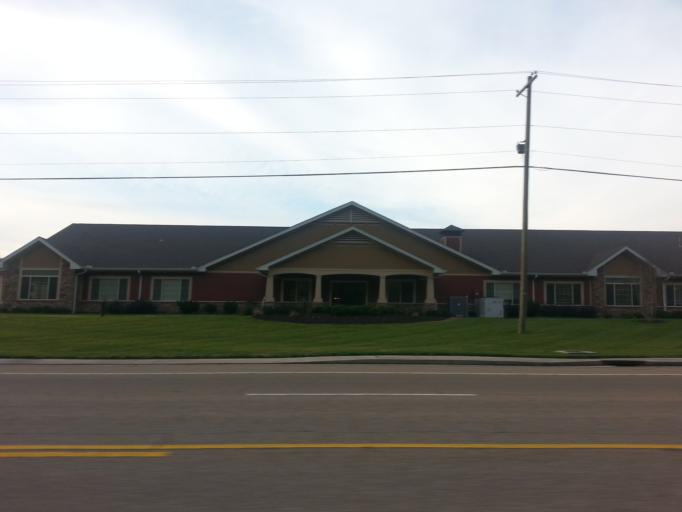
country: US
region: Tennessee
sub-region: Rhea County
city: Dayton
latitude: 35.5381
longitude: -84.9742
